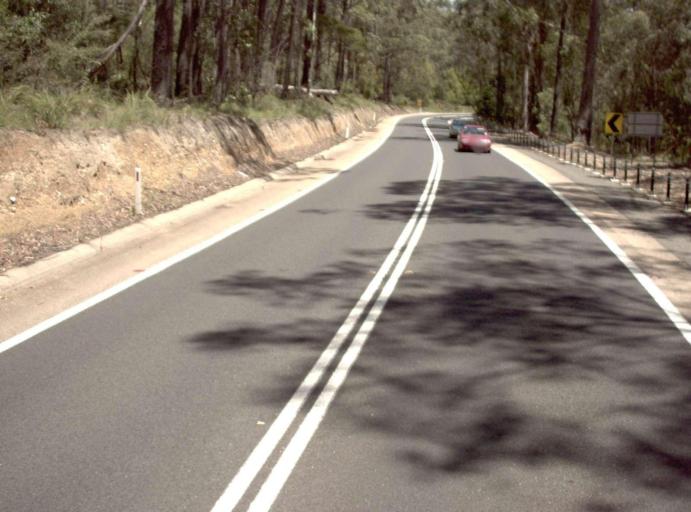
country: AU
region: Victoria
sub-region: East Gippsland
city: Lakes Entrance
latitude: -37.7041
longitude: 148.5774
